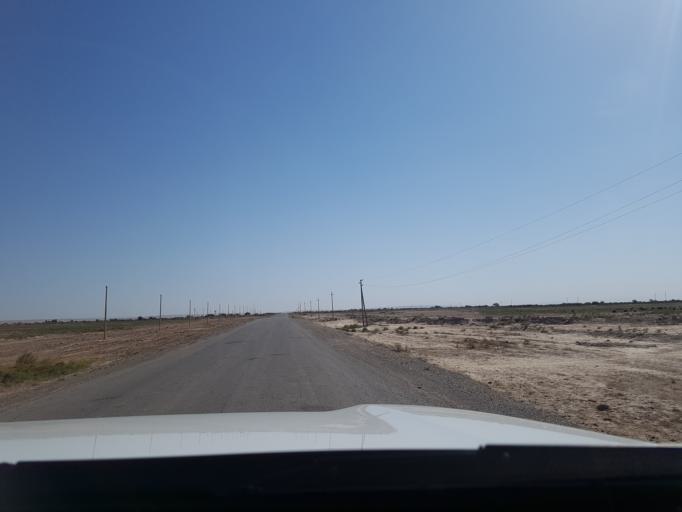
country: IR
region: Razavi Khorasan
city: Sarakhs
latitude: 36.5020
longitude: 61.2535
